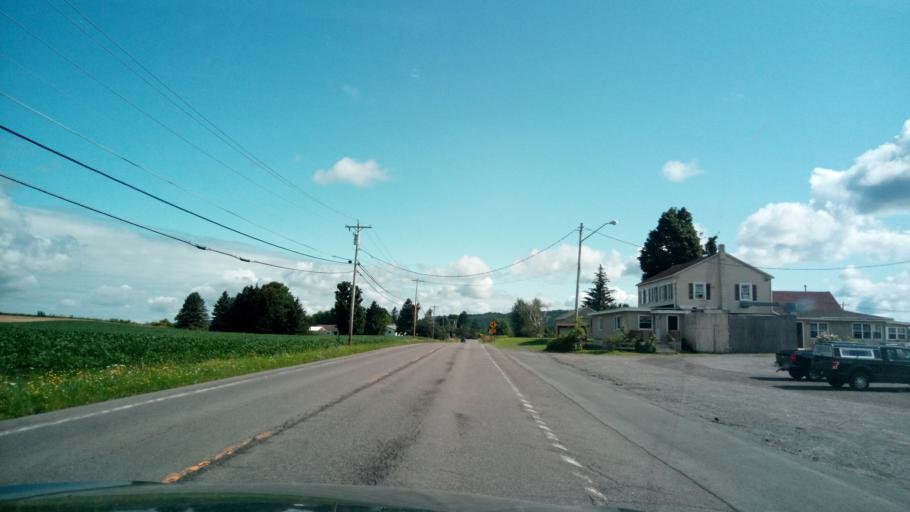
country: US
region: New York
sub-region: Onondaga County
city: Nedrow
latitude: 42.8140
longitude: -76.0796
